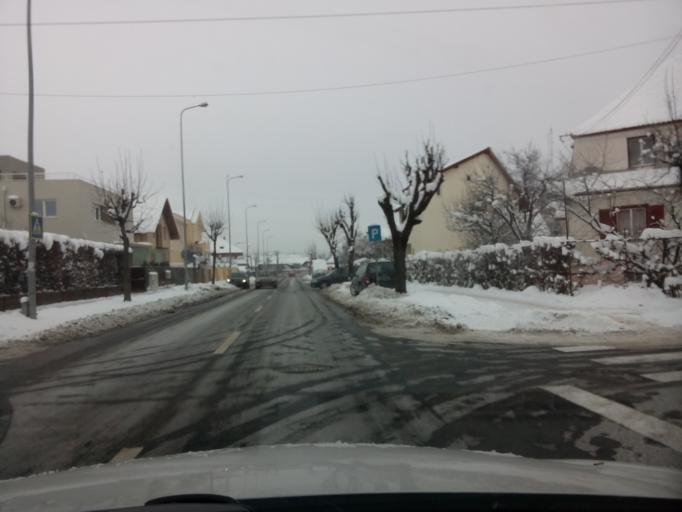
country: RO
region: Sibiu
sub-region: Municipiul Sibiu
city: Sibiu
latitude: 45.7885
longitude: 24.1635
